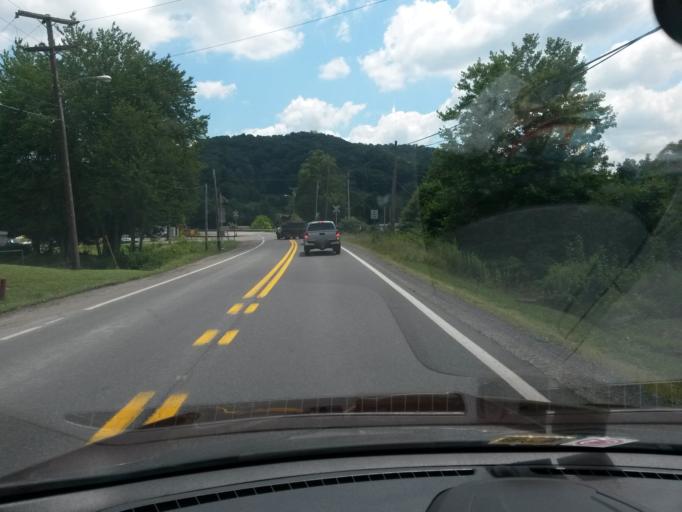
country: US
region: West Virginia
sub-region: Raleigh County
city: Sophia
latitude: 37.7289
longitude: -81.3054
